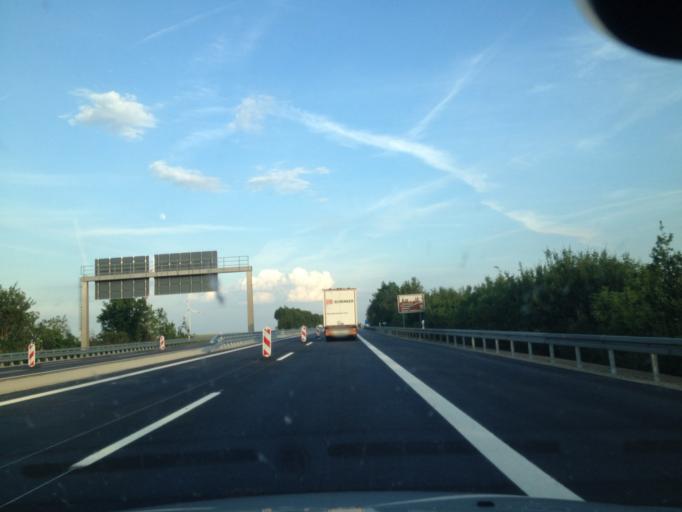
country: DE
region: Bavaria
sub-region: Regierungsbezirk Unterfranken
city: Biebelried
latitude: 49.7732
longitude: 10.0967
